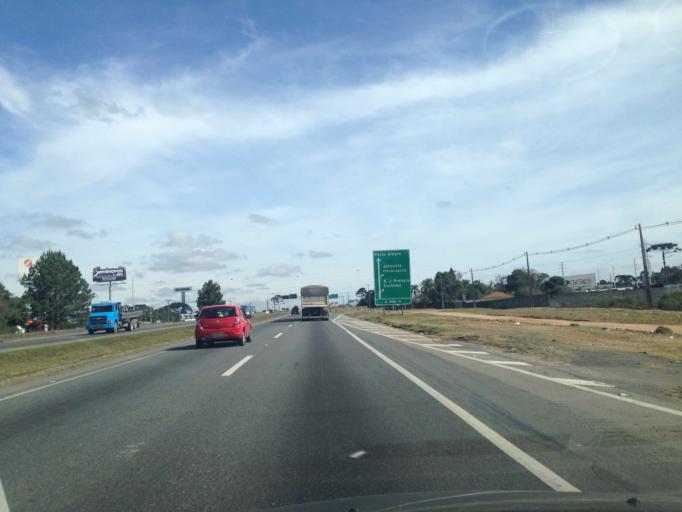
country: BR
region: Parana
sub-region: Sao Jose Dos Pinhais
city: Sao Jose dos Pinhais
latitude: -25.5668
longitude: -49.1702
